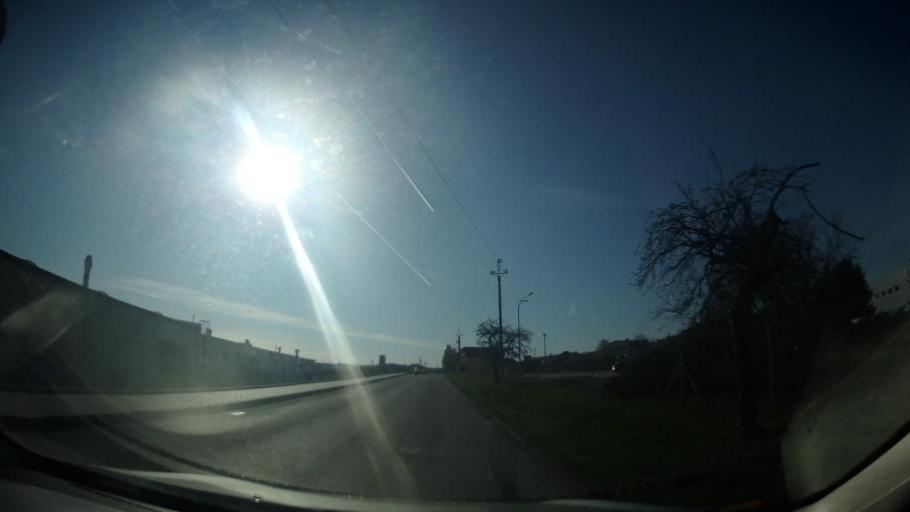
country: CZ
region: South Moravian
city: Moravany
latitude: 49.1445
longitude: 16.5937
